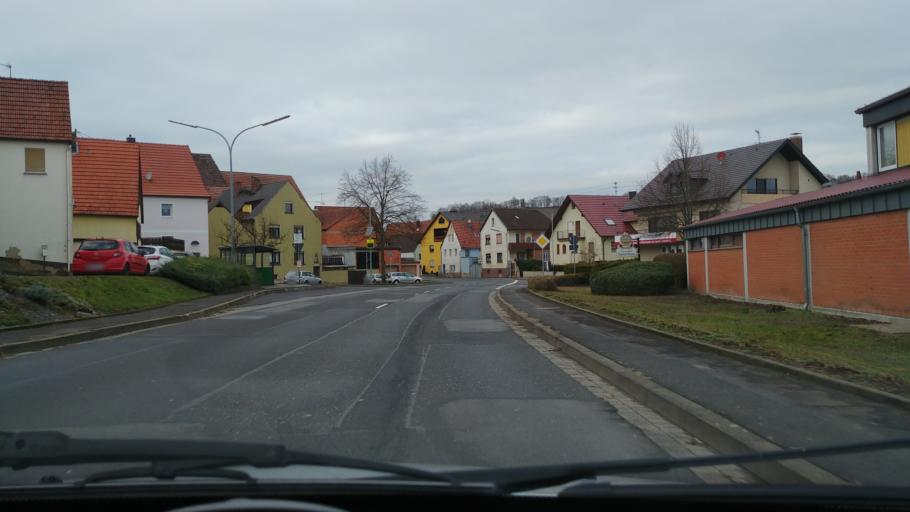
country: DE
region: Bavaria
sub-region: Regierungsbezirk Unterfranken
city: Thungen
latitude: 49.9447
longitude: 9.8365
